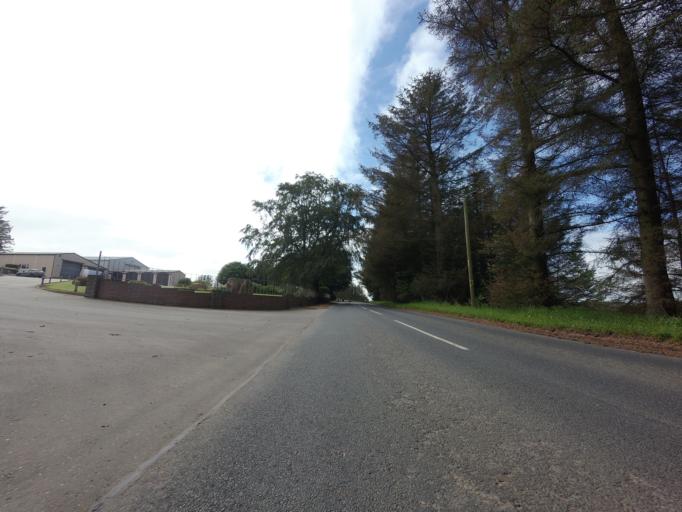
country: GB
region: Scotland
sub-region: Aberdeenshire
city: Turriff
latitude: 57.5430
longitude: -2.3153
